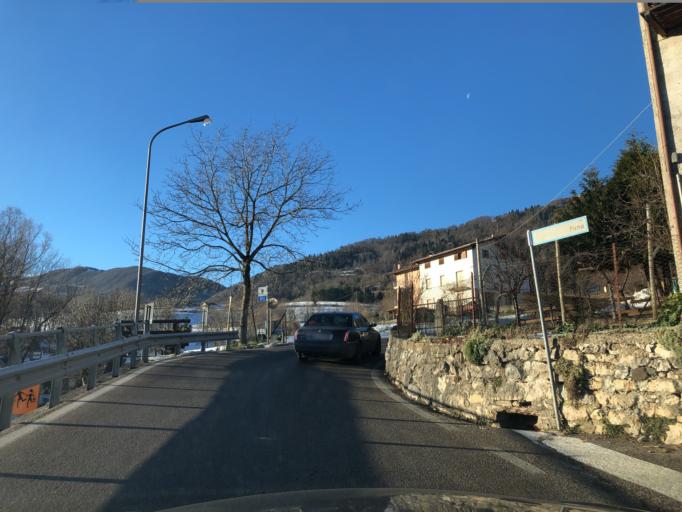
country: IT
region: Trentino-Alto Adige
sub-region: Provincia di Trento
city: Brentonico
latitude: 45.8145
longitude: 10.9464
